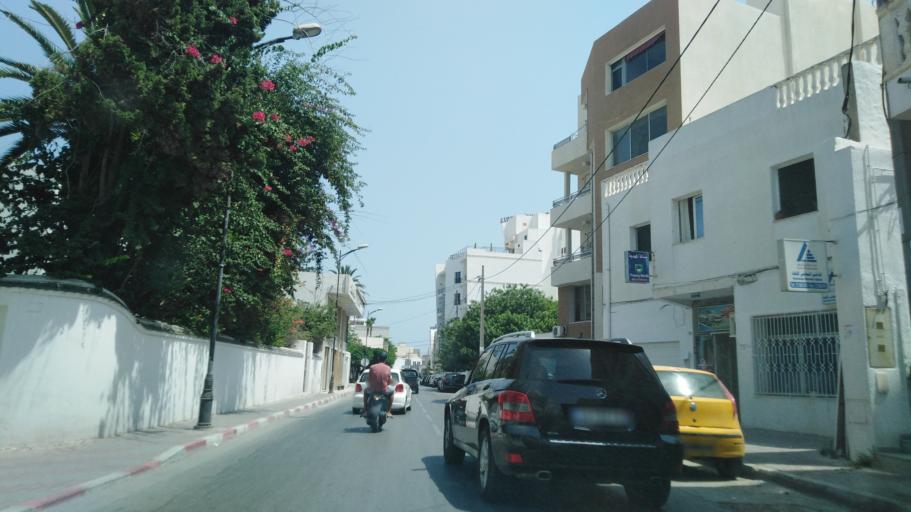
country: TN
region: Al Mahdiyah
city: Mahdia
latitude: 35.5059
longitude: 11.0609
